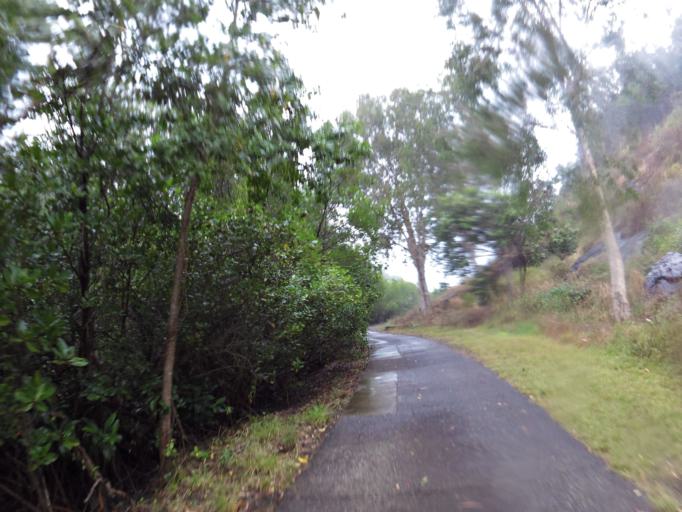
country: AU
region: Queensland
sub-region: Cairns
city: Cairns
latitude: -16.8948
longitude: 145.7525
